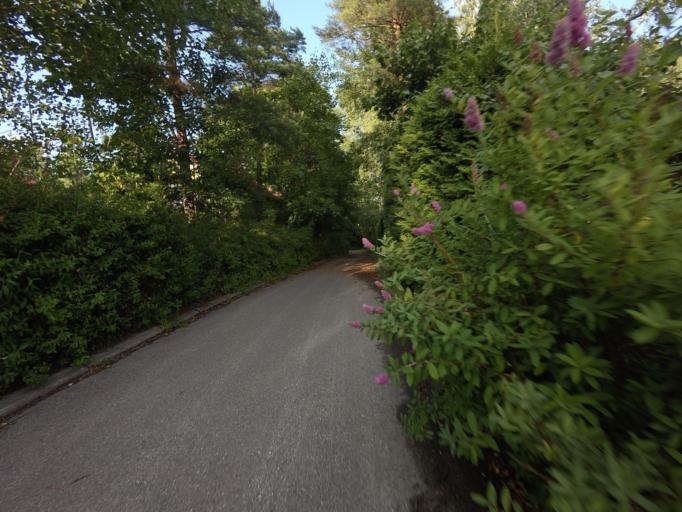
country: FI
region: Uusimaa
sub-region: Helsinki
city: Espoo
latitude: 60.1611
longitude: 24.6743
